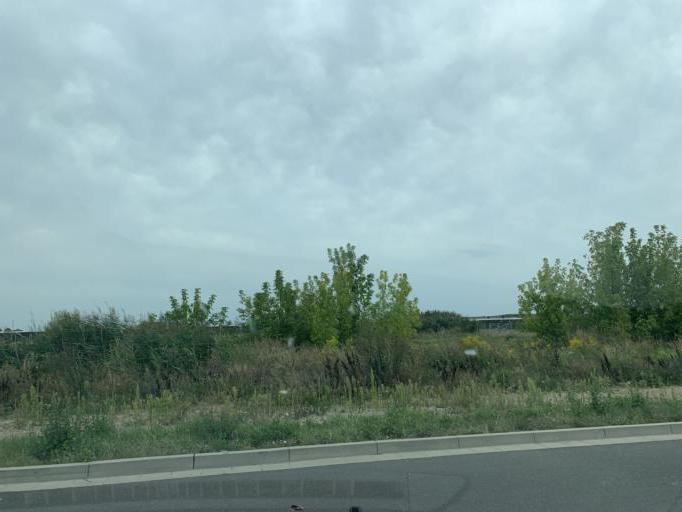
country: DE
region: Brandenburg
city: Velten
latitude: 52.7112
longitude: 13.1172
